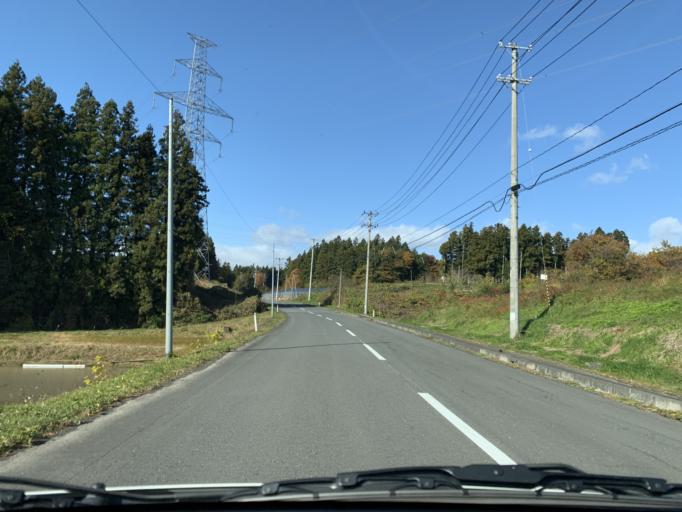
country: JP
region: Iwate
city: Mizusawa
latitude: 39.0256
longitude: 141.1099
